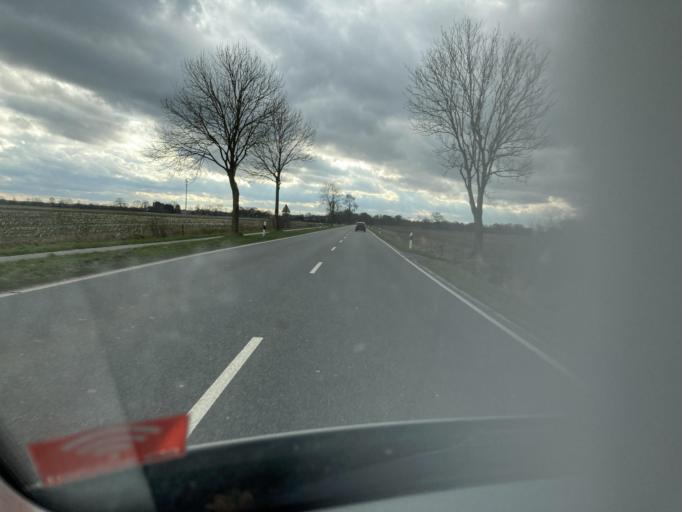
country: DE
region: Lower Saxony
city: Zetel
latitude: 53.4660
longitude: 7.9527
